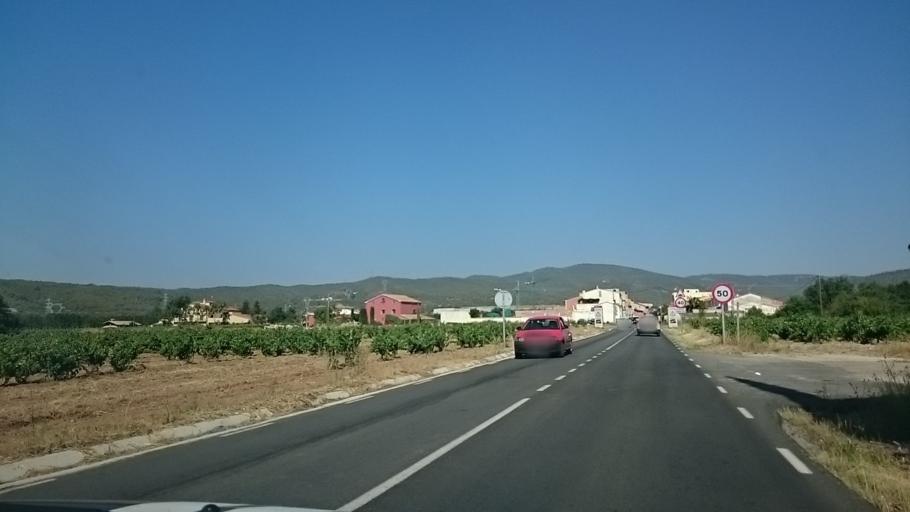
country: ES
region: Catalonia
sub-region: Provincia de Barcelona
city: Sant Marti Sarroca
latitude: 41.3838
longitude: 1.5892
